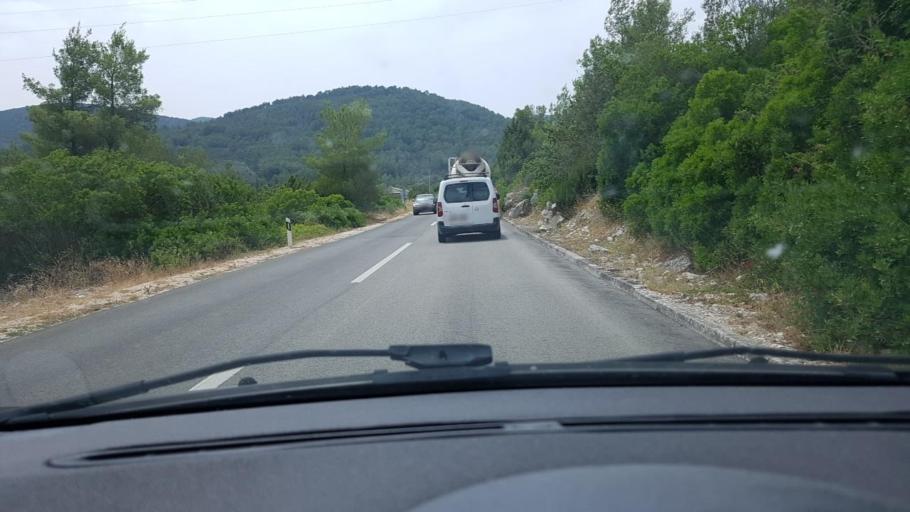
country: HR
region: Dubrovacko-Neretvanska
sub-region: Grad Dubrovnik
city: Vela Luka
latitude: 42.9501
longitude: 16.7817
